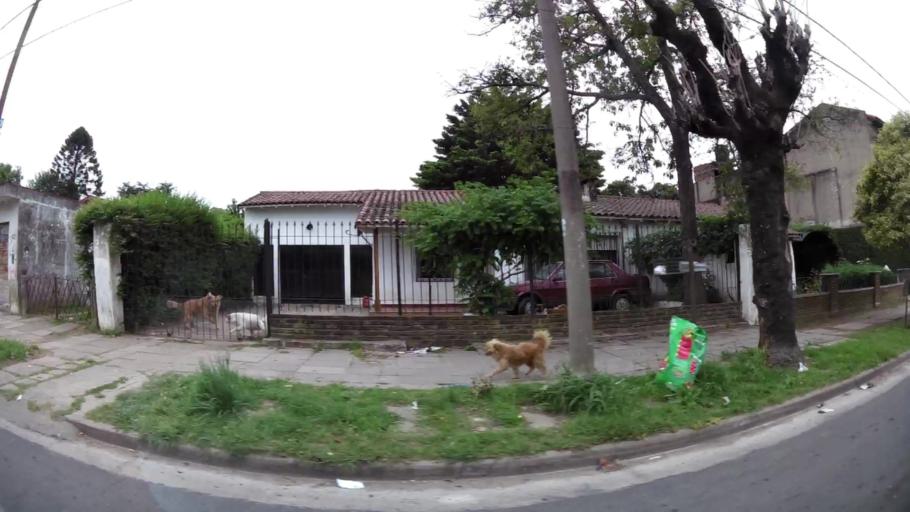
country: AR
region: Buenos Aires
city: San Justo
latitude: -34.7066
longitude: -58.5400
